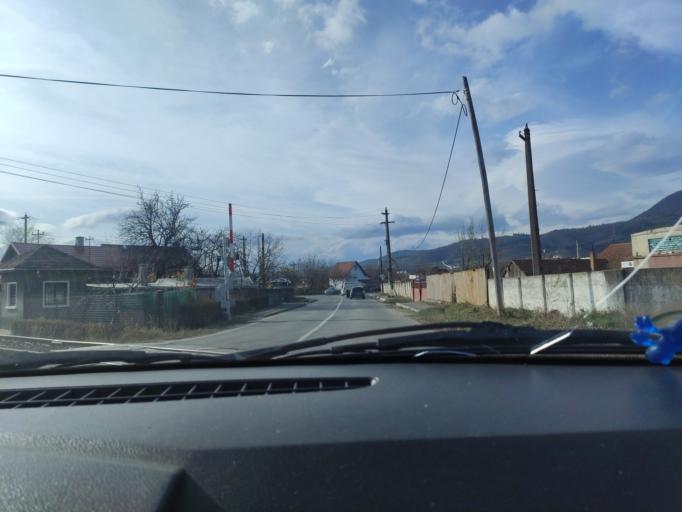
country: RO
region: Brasov
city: Codlea
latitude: 45.7049
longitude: 25.4575
